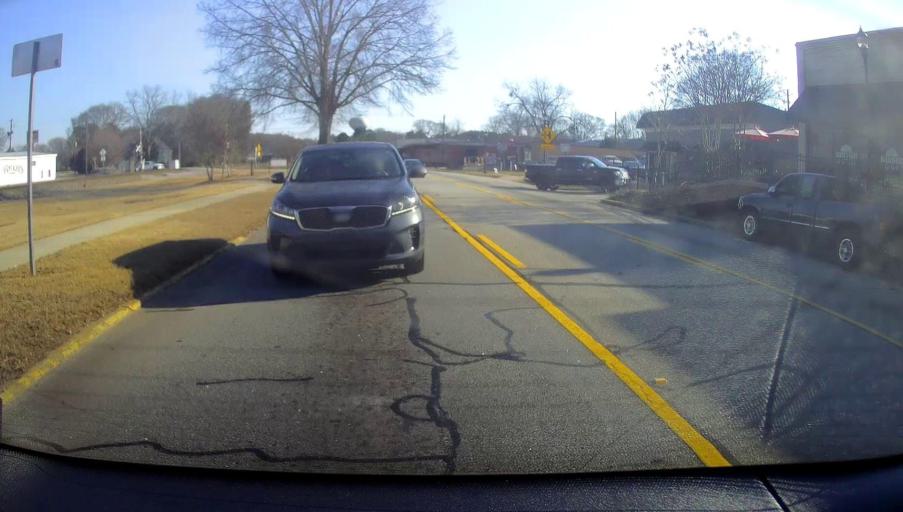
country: US
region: Georgia
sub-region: Henry County
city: Locust Grove
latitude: 33.3466
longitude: -84.1097
